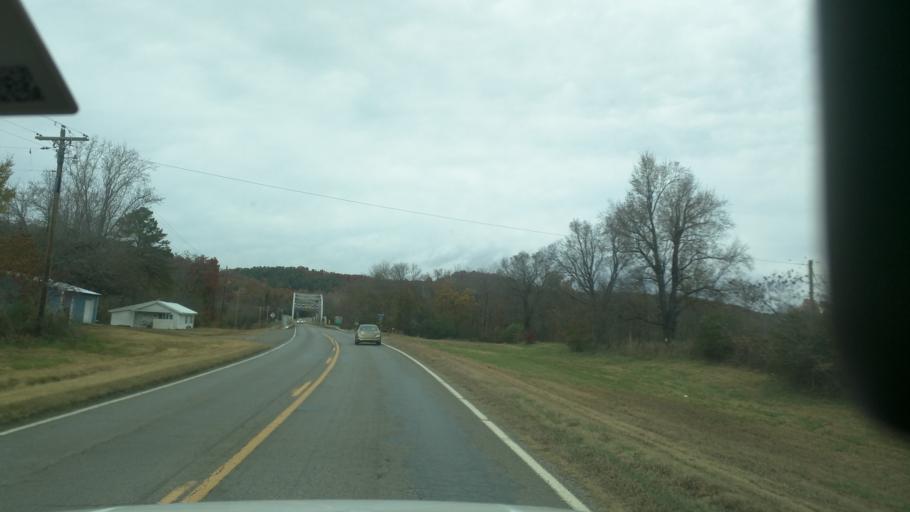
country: US
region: Oklahoma
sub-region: Cherokee County
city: Tahlequah
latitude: 35.9197
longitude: -94.8364
